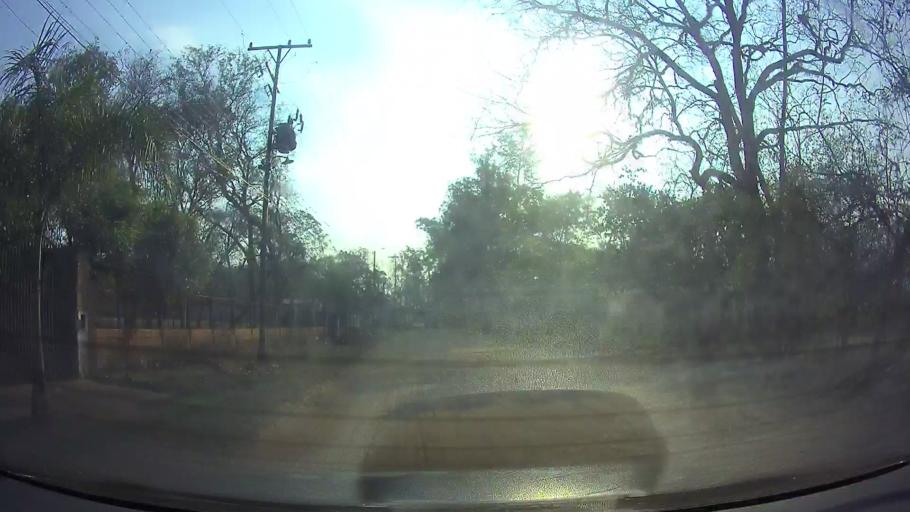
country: PY
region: Central
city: Limpio
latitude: -25.2191
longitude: -57.5009
